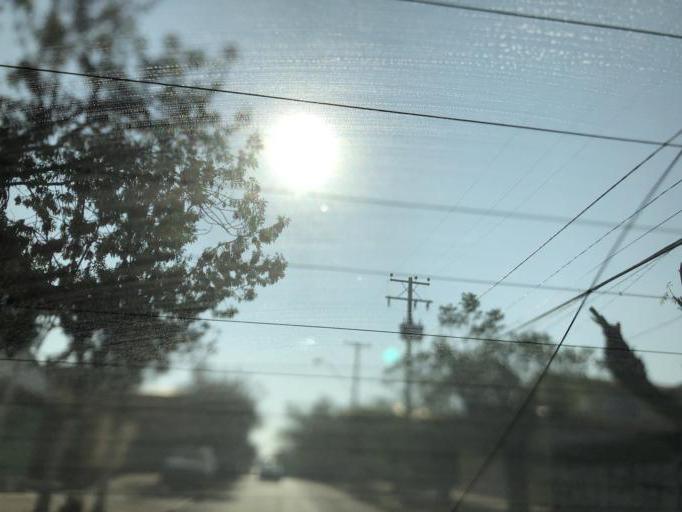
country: CL
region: Santiago Metropolitan
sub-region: Provincia de Cordillera
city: Puente Alto
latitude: -33.6129
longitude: -70.5511
